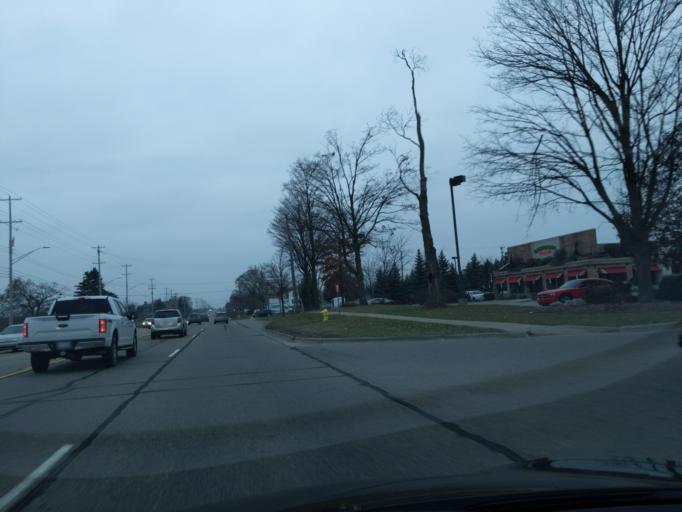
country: US
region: Michigan
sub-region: Eaton County
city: Waverly
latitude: 42.7412
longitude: -84.6458
